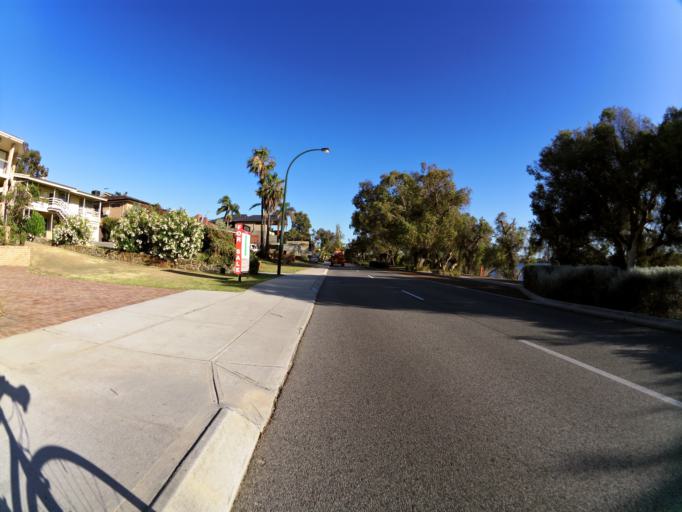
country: AU
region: Western Australia
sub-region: Melville
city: Mount Pleasant
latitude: -32.0349
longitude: 115.8540
